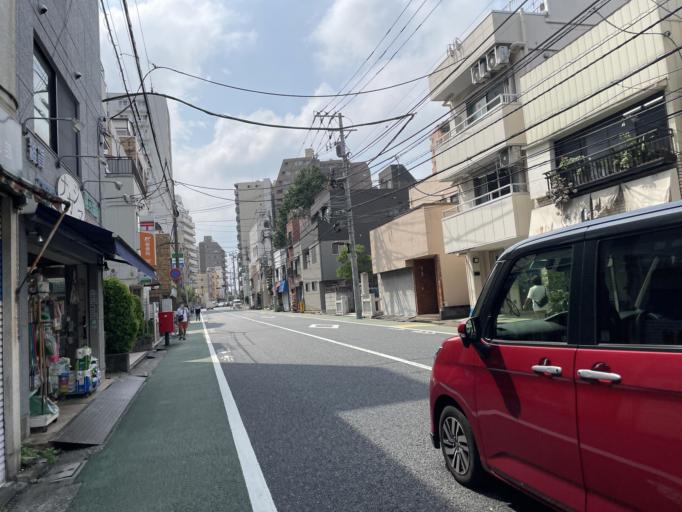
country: JP
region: Tokyo
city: Tokyo
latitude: 35.7238
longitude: 139.7555
